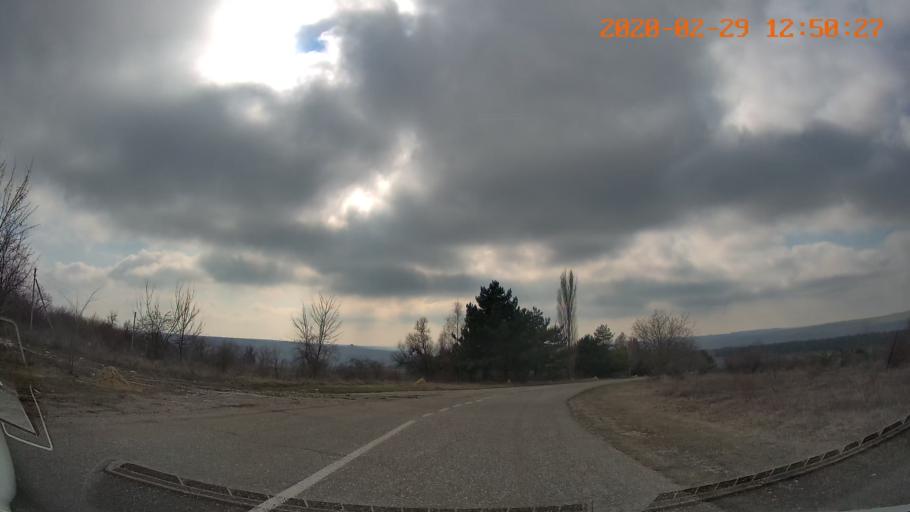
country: MD
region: Telenesti
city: Camenca
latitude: 48.1241
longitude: 28.7388
